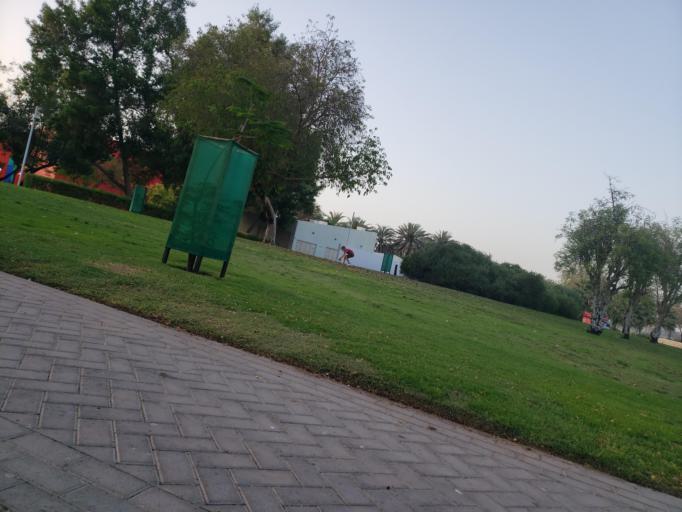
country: AE
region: Ash Shariqah
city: Sharjah
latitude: 25.2345
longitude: 55.3291
